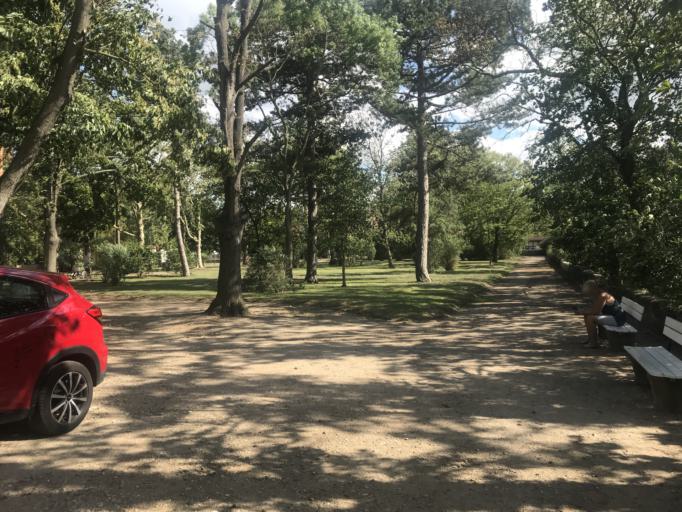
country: DE
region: Saxony-Anhalt
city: Bad Durrenberg
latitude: 51.2937
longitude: 12.0621
